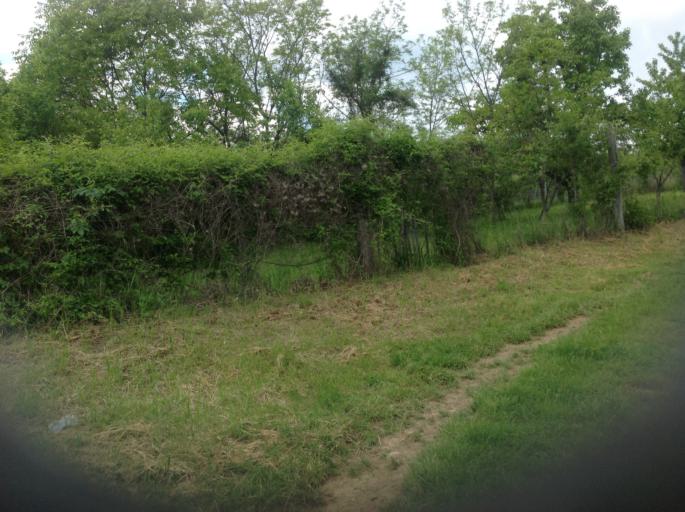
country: HU
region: Komarom-Esztergom
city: Kesztolc
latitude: 47.7151
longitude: 18.8039
